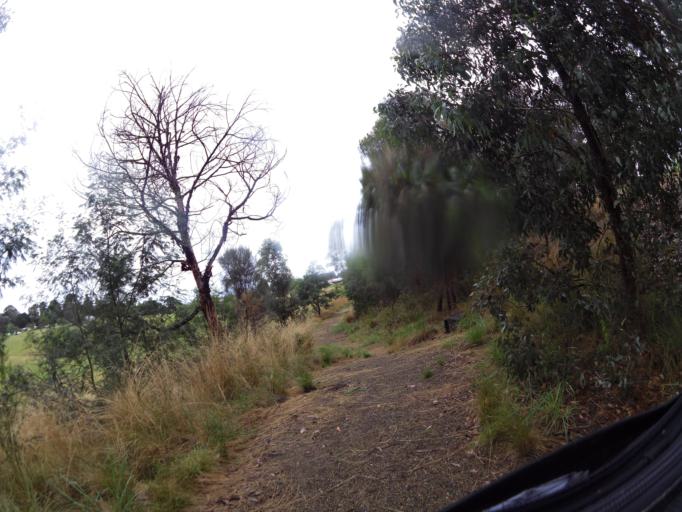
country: AU
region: Victoria
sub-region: East Gippsland
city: Bairnsdale
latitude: -37.8115
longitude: 147.7441
